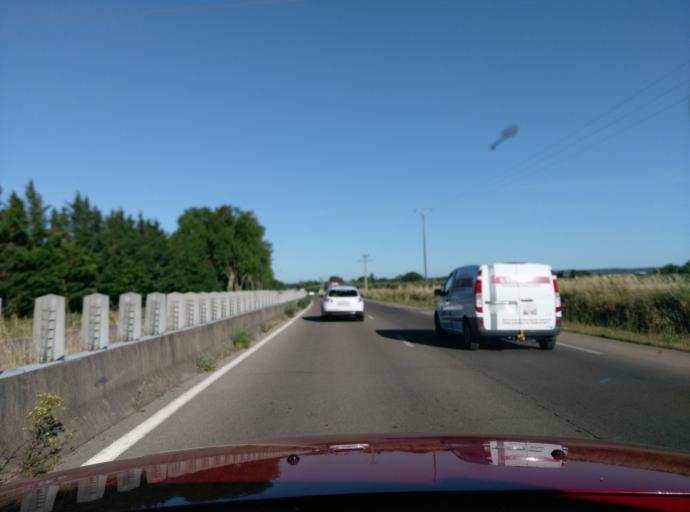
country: FR
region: Languedoc-Roussillon
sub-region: Departement du Gard
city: Rodilhan
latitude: 43.8310
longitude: 4.4490
